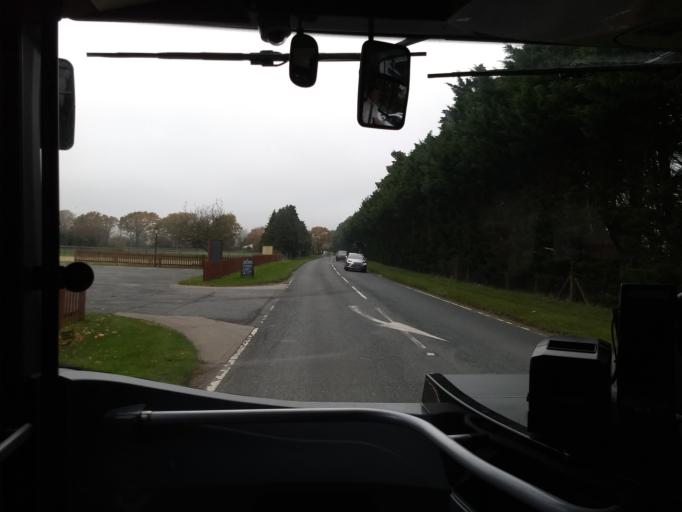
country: GB
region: England
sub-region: Isle of Wight
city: Newchurch
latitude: 50.6548
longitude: -1.2227
